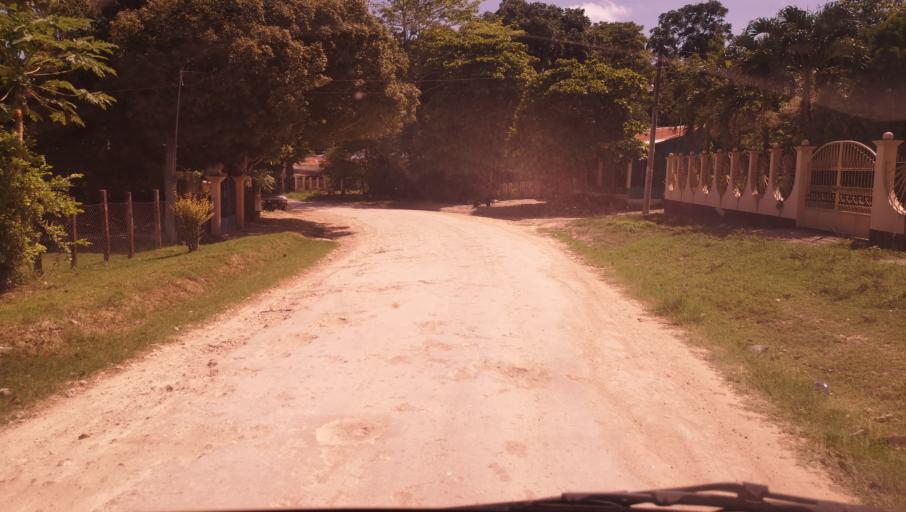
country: GT
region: Peten
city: Melchor de Mencos
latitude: 16.9750
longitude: -89.2634
